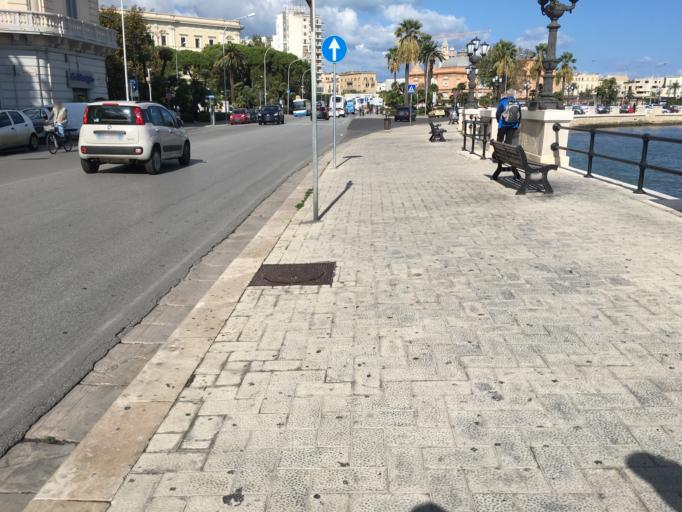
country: IT
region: Apulia
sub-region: Provincia di Bari
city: Bari
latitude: 41.1245
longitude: 16.8752
